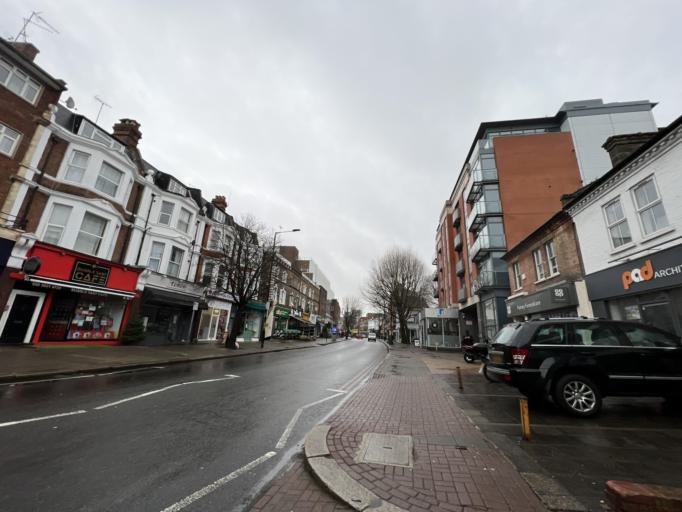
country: GB
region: England
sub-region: Greater London
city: Wandsworth
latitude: 51.4620
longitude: -0.2215
